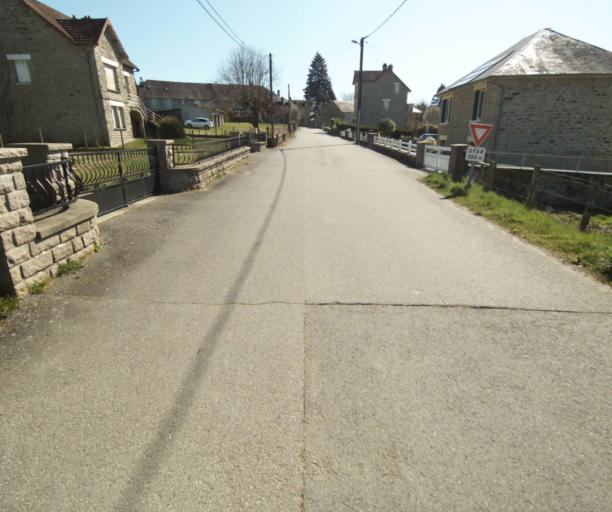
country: FR
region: Limousin
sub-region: Departement de la Correze
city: Chamboulive
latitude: 45.4679
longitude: 1.7373
